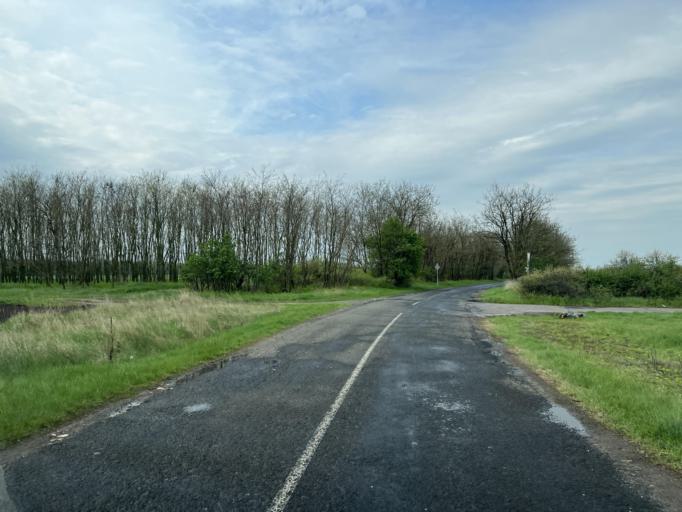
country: HU
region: Pest
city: Danszentmiklos
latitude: 47.1792
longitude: 19.5328
